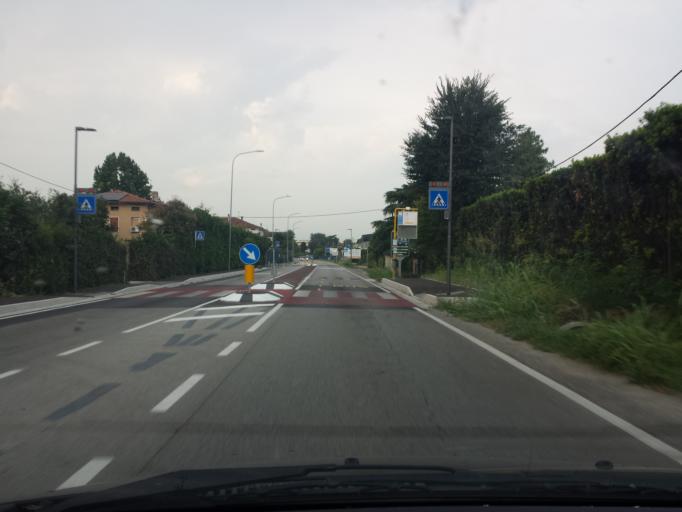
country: IT
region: Veneto
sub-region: Provincia di Vicenza
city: Monticello Conte Otto
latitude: 45.5842
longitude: 11.5550
